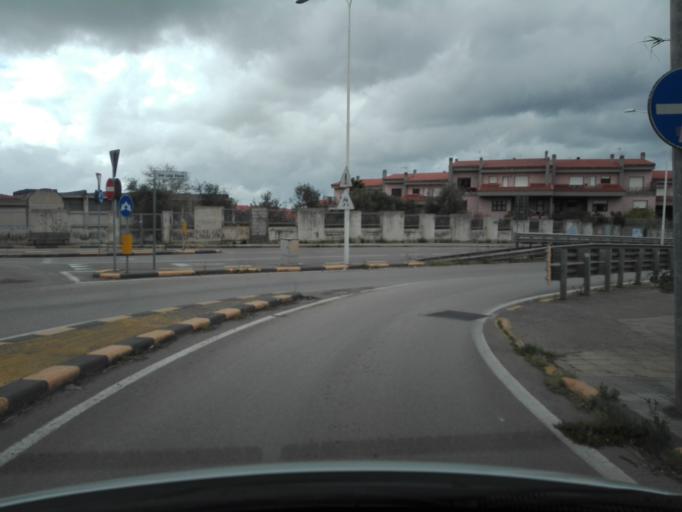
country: IT
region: Sardinia
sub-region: Provincia di Sassari
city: Sassari
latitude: 40.7286
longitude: 8.5757
